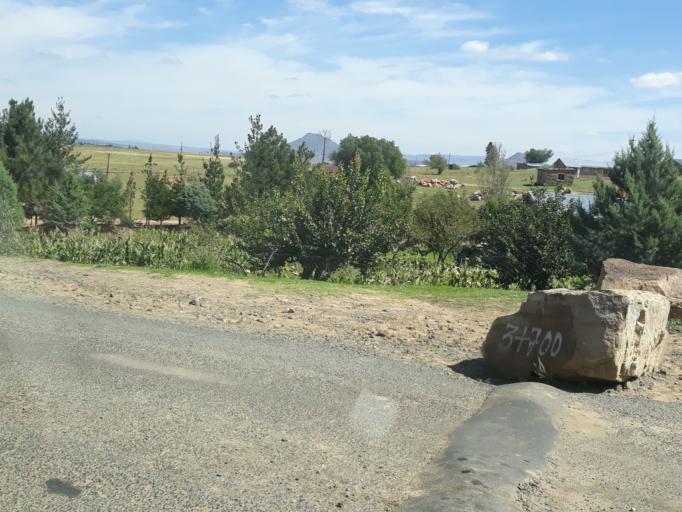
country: LS
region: Mohale's Hoek District
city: Mohale's Hoek
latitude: -30.1017
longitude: 27.4786
